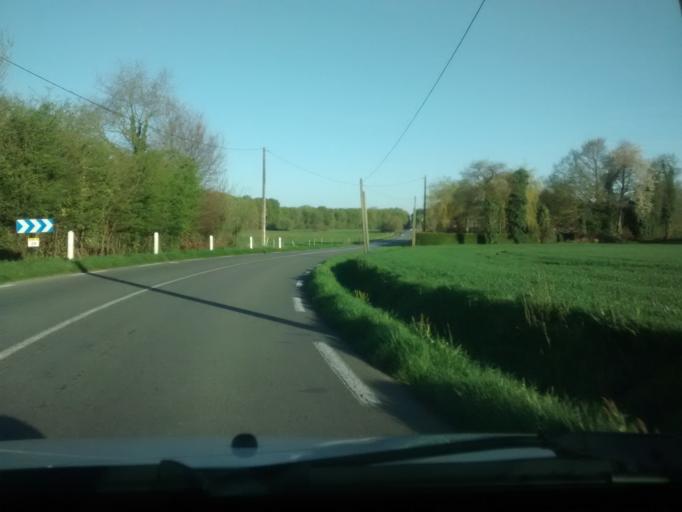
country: FR
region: Brittany
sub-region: Departement d'Ille-et-Vilaine
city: Antrain
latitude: 48.4675
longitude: -1.5291
